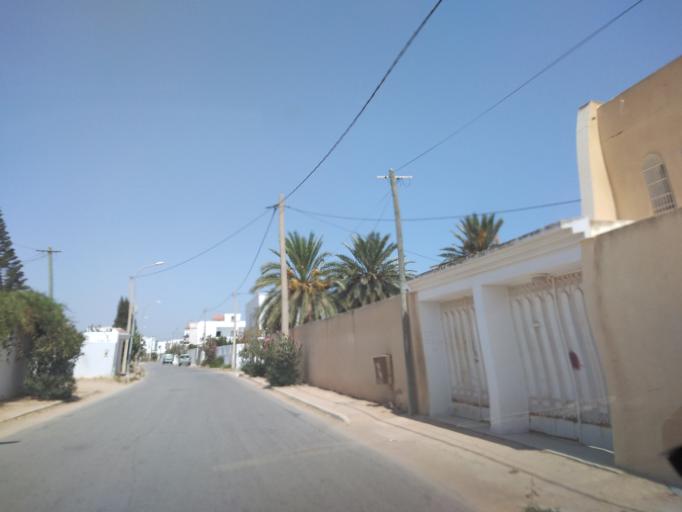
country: TN
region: Safaqis
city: Sfax
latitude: 34.7546
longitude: 10.7394
